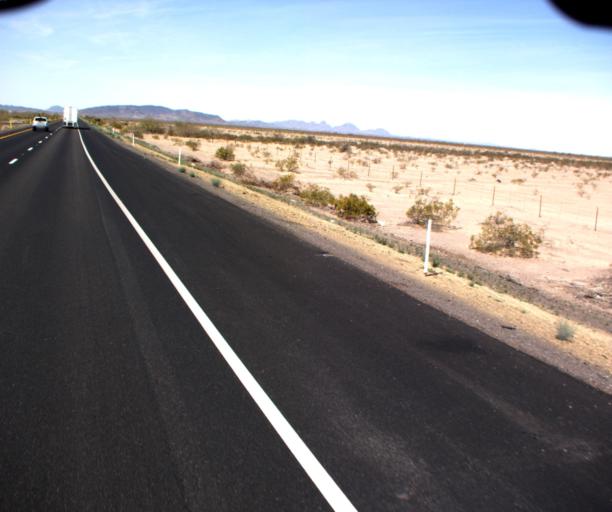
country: US
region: Arizona
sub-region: La Paz County
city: Salome
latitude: 33.6323
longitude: -113.7746
